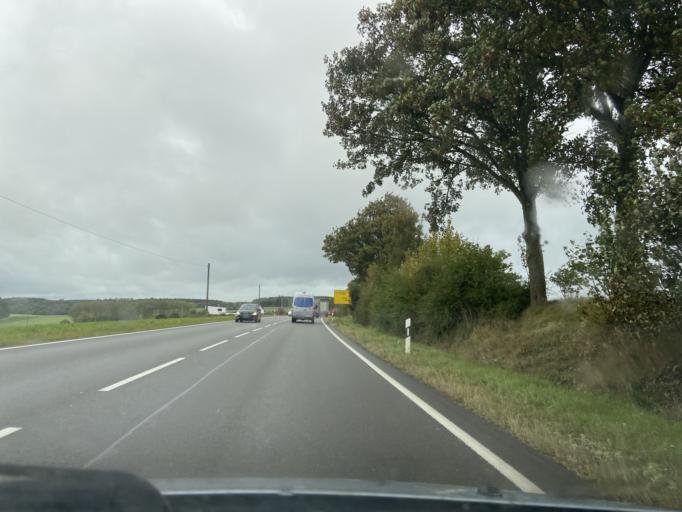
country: DE
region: Baden-Wuerttemberg
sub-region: Freiburg Region
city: Buchheim
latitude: 47.9835
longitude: 9.0445
